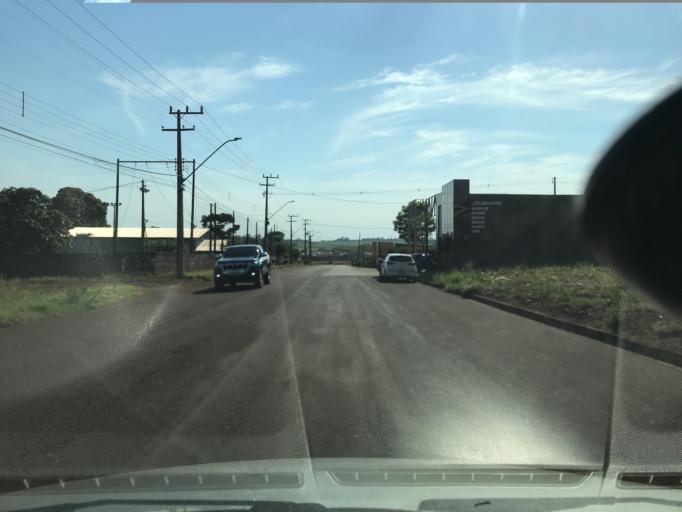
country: BR
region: Parana
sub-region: Palotina
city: Palotina
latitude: -24.2952
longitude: -53.8328
